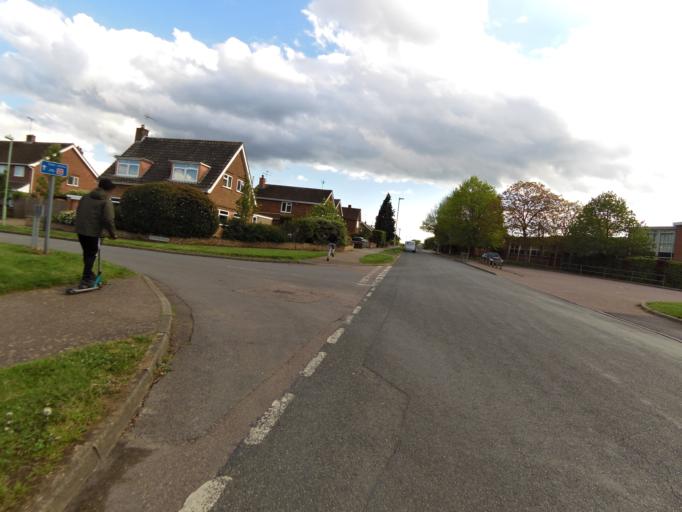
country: GB
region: England
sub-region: Suffolk
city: Stowmarket
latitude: 52.1917
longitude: 0.9806
